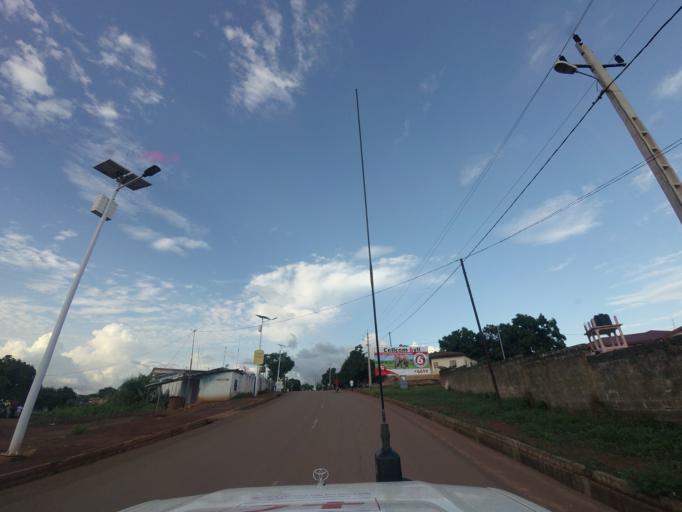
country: GN
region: Nzerekore
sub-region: Nzerekore Prefecture
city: Nzerekore
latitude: 7.7382
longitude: -8.8211
